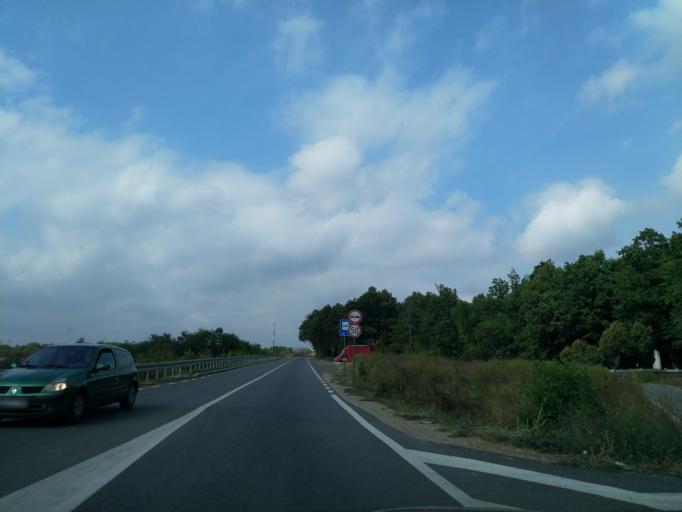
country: RS
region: Central Serbia
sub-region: Sumadijski Okrug
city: Kragujevac
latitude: 44.0577
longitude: 20.8940
